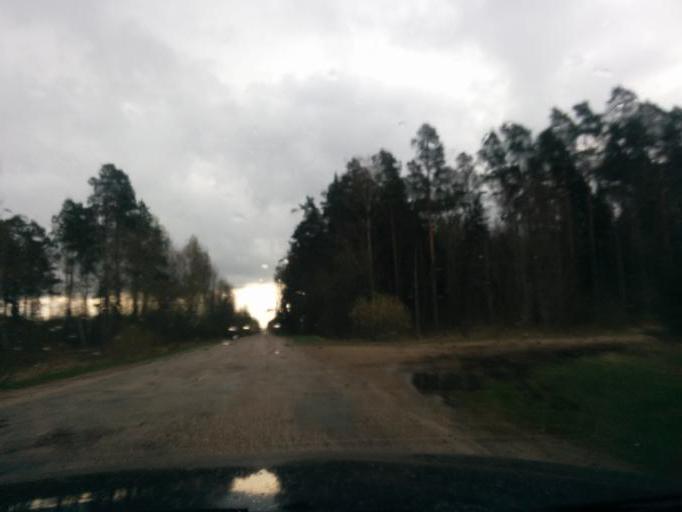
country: LT
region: Siauliu apskritis
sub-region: Joniskis
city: Joniskis
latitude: 56.4170
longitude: 23.6586
